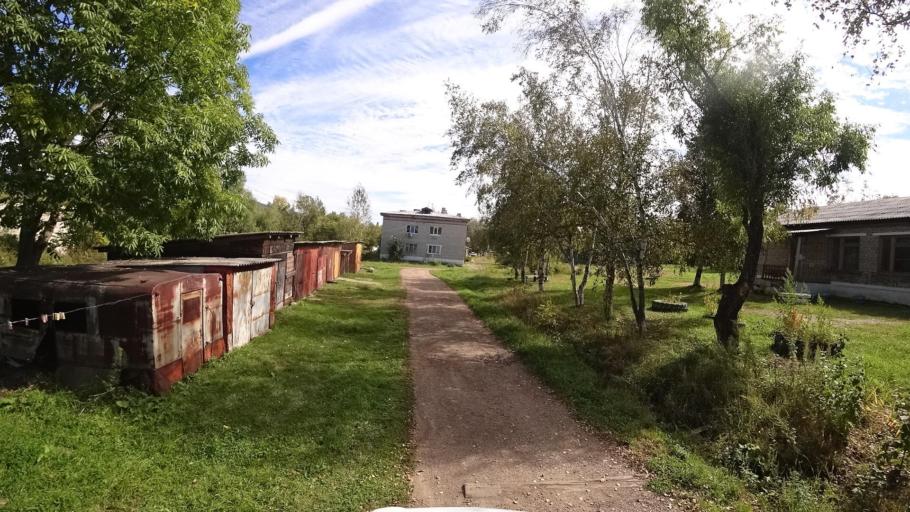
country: RU
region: Primorskiy
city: Yakovlevka
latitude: 44.4004
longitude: 133.5999
